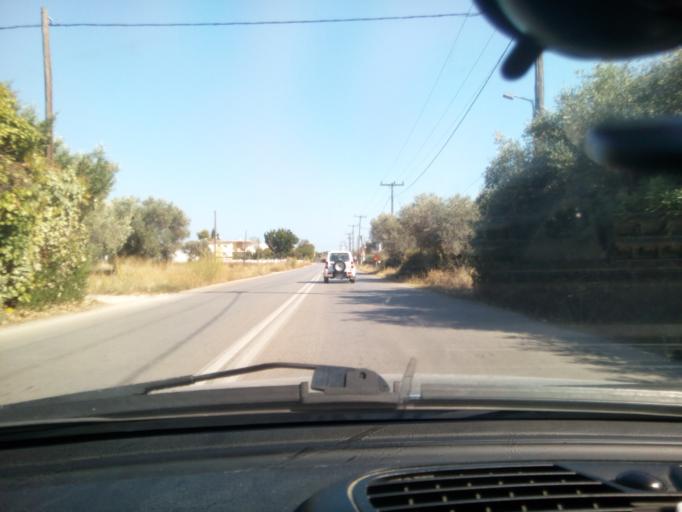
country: GR
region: Central Greece
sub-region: Nomos Evvoias
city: Malakonta
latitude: 38.4022
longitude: 23.7541
